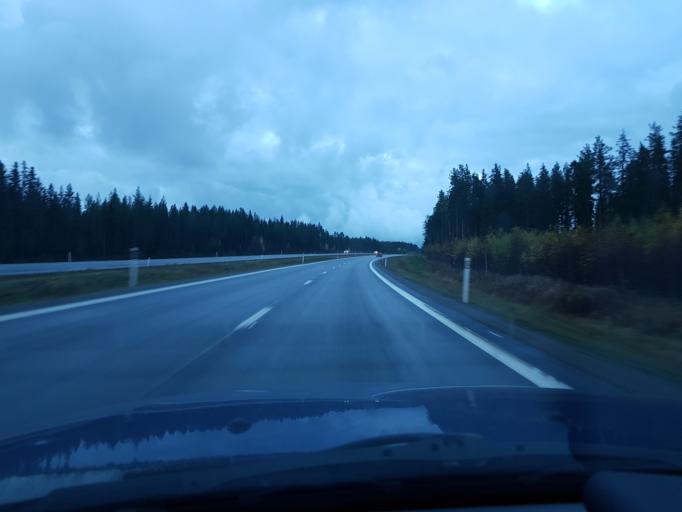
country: SE
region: Vaesterbotten
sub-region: Skelleftea Kommun
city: Backa
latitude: 64.9225
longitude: 21.1060
